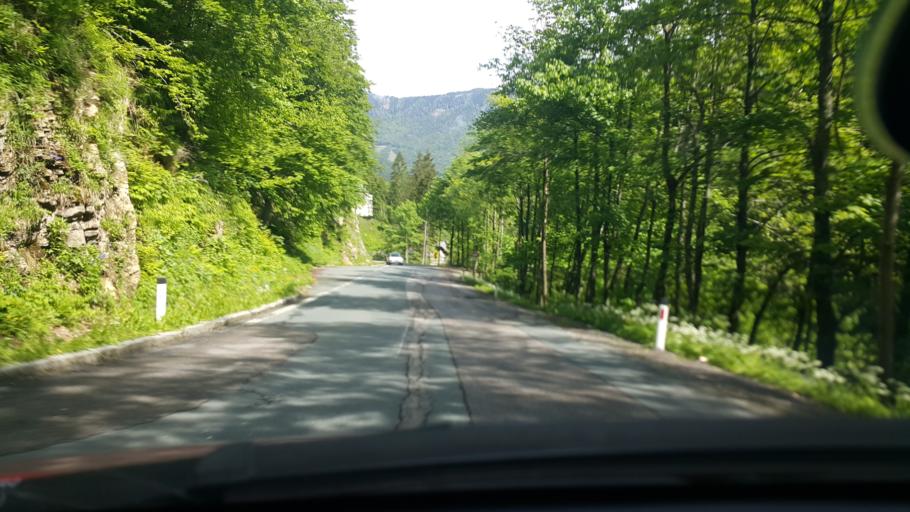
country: AT
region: Carinthia
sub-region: Politischer Bezirk Klagenfurt Land
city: Ferlach
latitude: 46.4625
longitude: 14.2578
